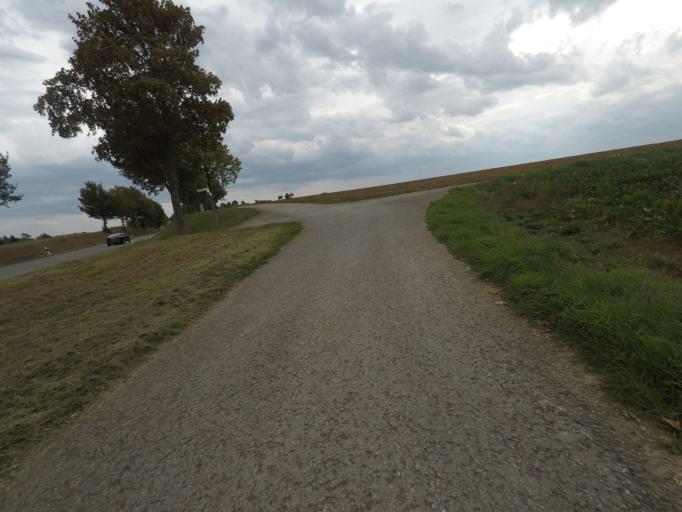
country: DE
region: Baden-Wuerttemberg
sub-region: Regierungsbezirk Stuttgart
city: Herrenberg
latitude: 48.5525
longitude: 8.9068
